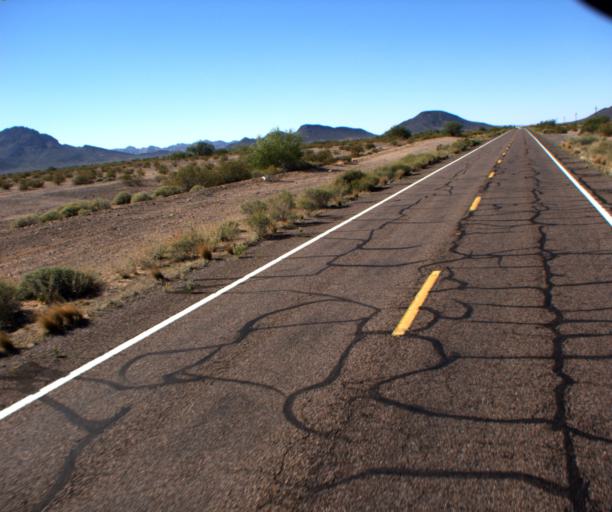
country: US
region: Arizona
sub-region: Maricopa County
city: Gila Bend
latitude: 32.8009
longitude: -112.7991
